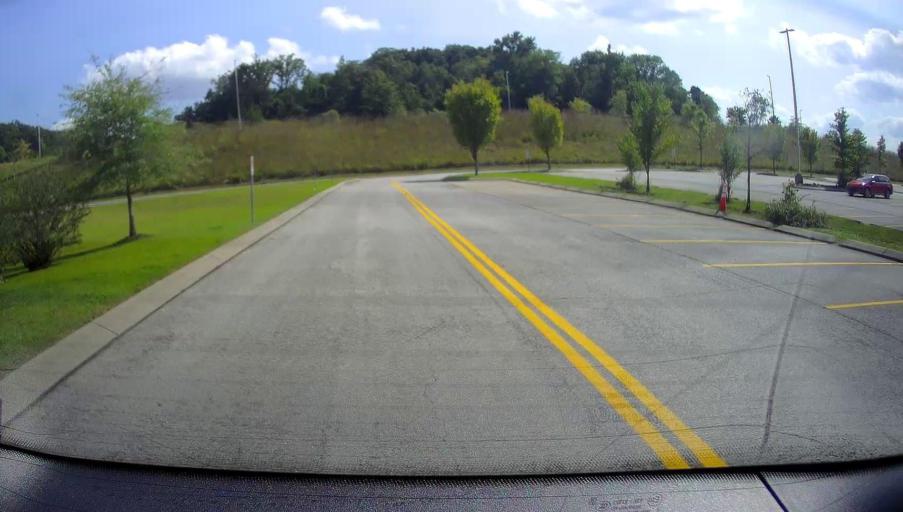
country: US
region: Tennessee
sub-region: Hamilton County
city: Harrison
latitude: 35.0766
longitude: -85.1290
